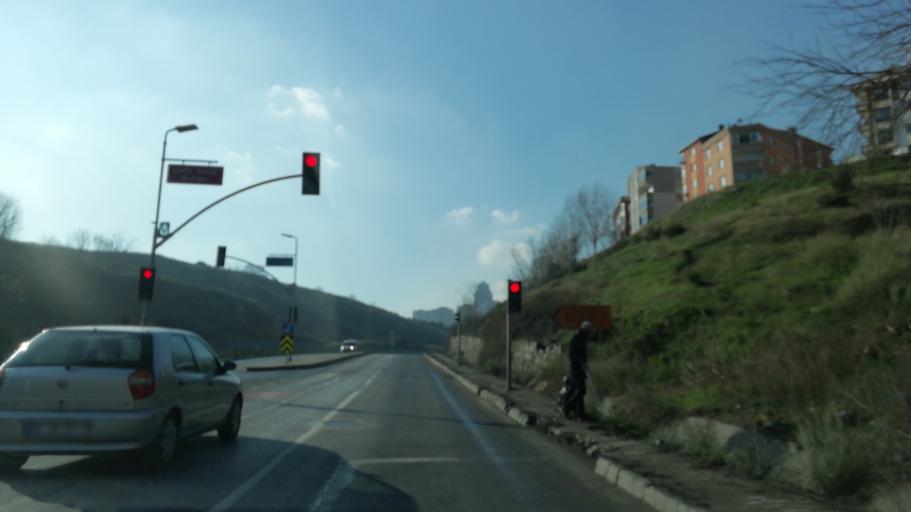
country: TR
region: Istanbul
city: Sultangazi
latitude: 41.0953
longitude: 28.9116
